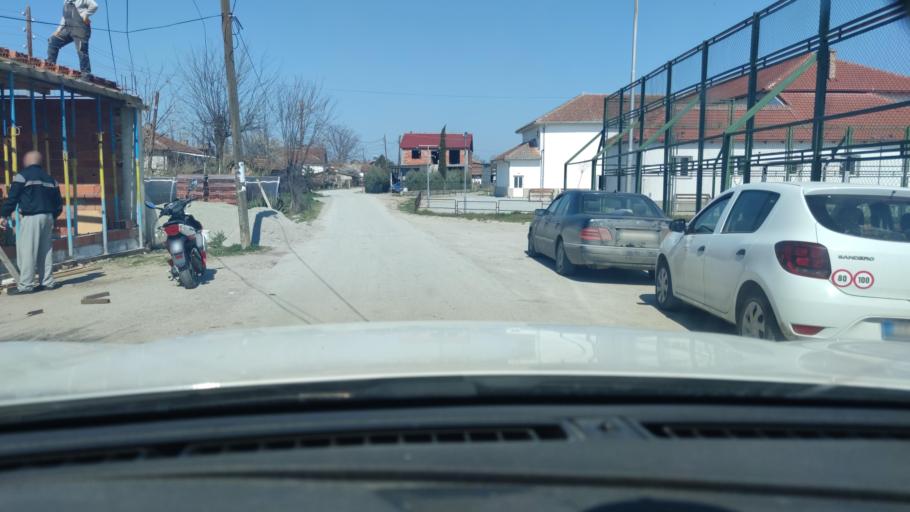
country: MK
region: Rosoman
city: Rosoman
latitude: 41.5180
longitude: 21.9404
